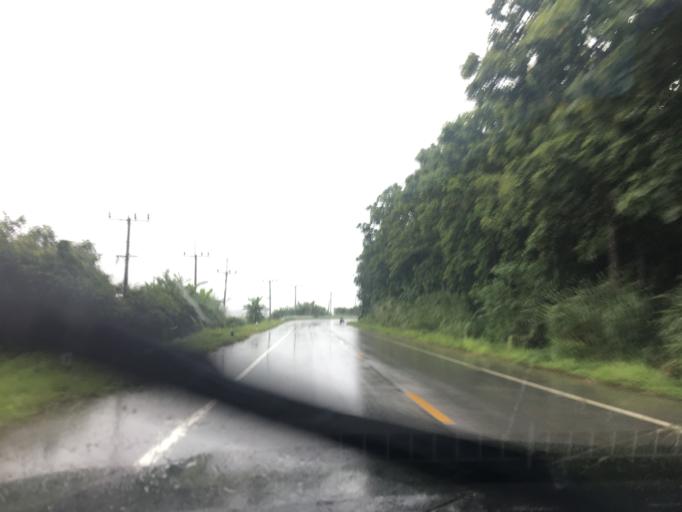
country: TH
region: Chiang Rai
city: Chiang Saen
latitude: 20.2767
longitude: 100.2045
